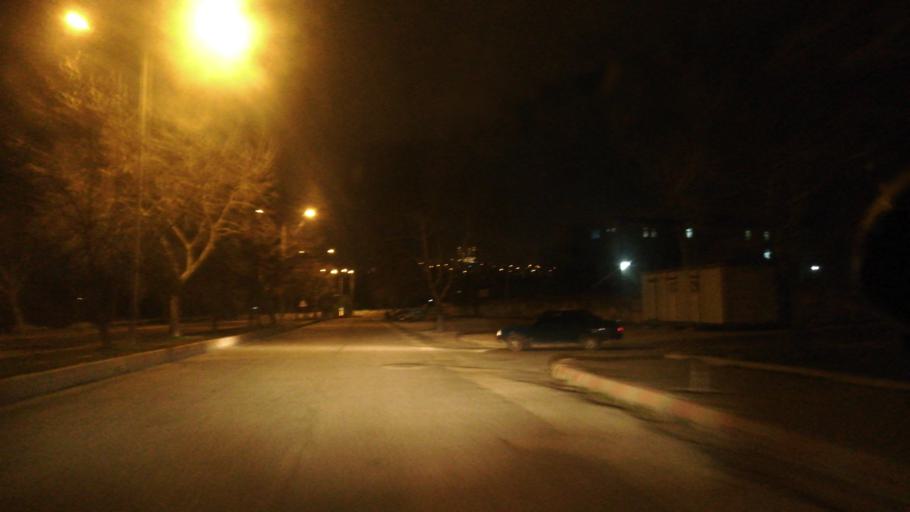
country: TR
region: Kahramanmaras
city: Kahramanmaras
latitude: 37.5768
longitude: 36.9412
